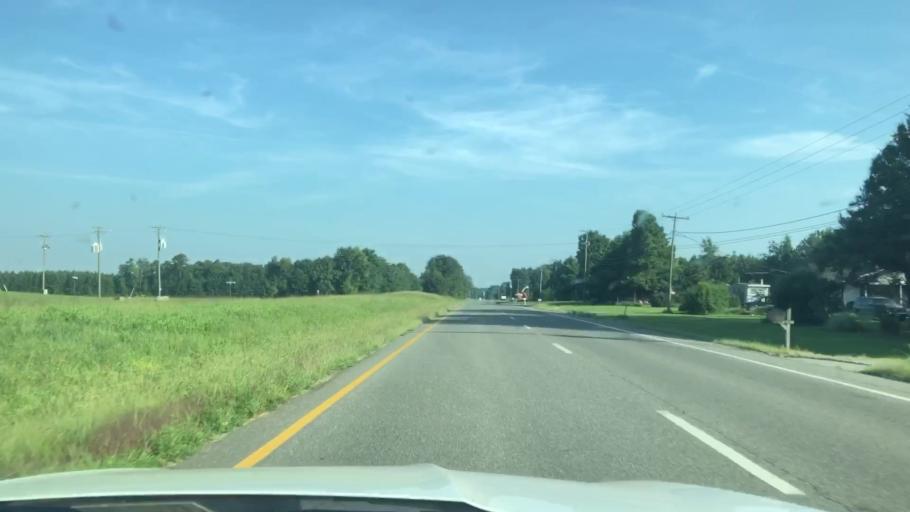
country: US
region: Virginia
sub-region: Middlesex County
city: Saluda
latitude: 37.7057
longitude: -76.6893
